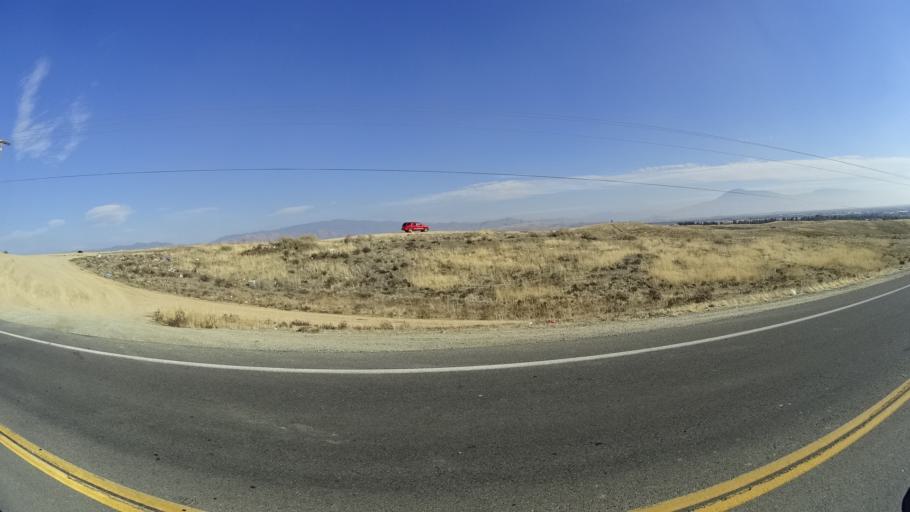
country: US
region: California
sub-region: Kern County
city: Bakersfield
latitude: 35.3907
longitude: -118.9143
